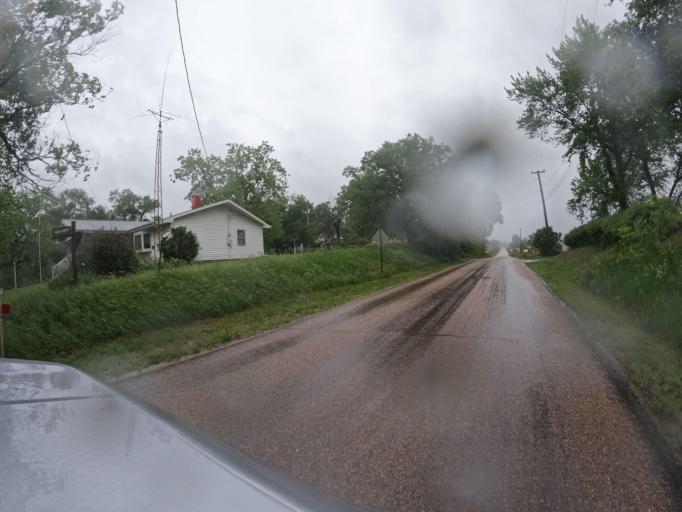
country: US
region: Nebraska
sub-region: Gage County
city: Wymore
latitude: 40.1235
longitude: -96.6531
